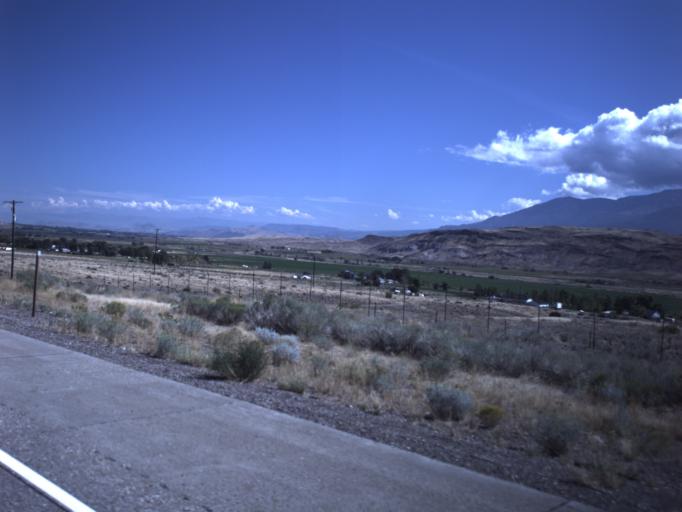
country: US
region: Utah
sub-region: Sevier County
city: Monroe
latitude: 38.6082
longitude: -112.2327
